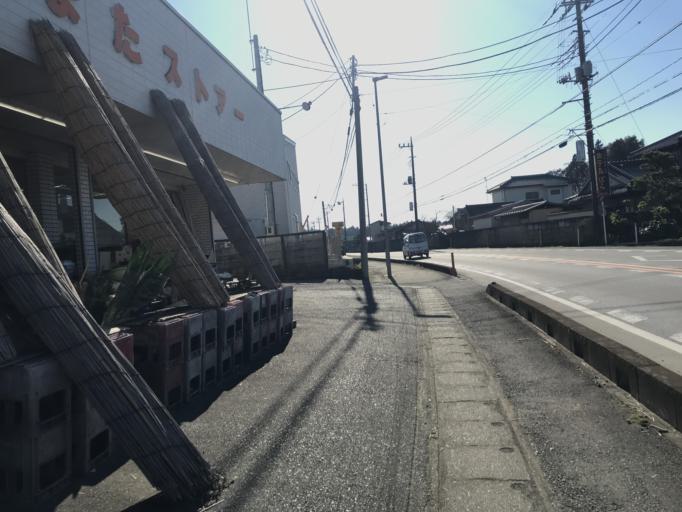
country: JP
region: Ibaraki
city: Sakai
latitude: 36.1576
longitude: 139.8099
